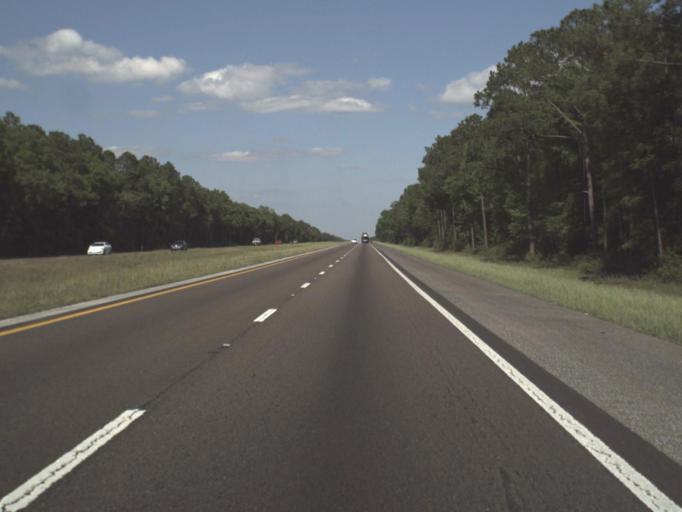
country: US
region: Florida
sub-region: Santa Rosa County
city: East Milton
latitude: 30.6505
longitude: -86.8892
